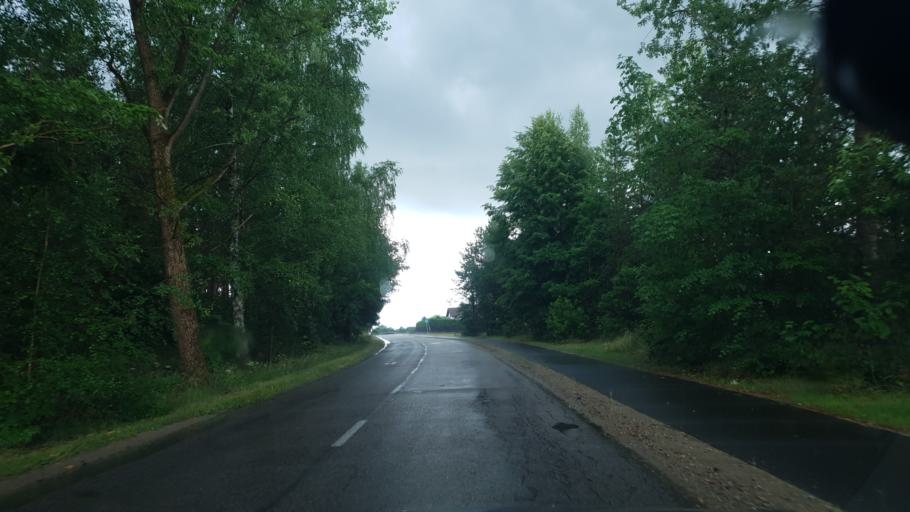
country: PL
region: Pomeranian Voivodeship
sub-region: Powiat kartuski
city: Stezyca
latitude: 54.2139
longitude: 17.9592
